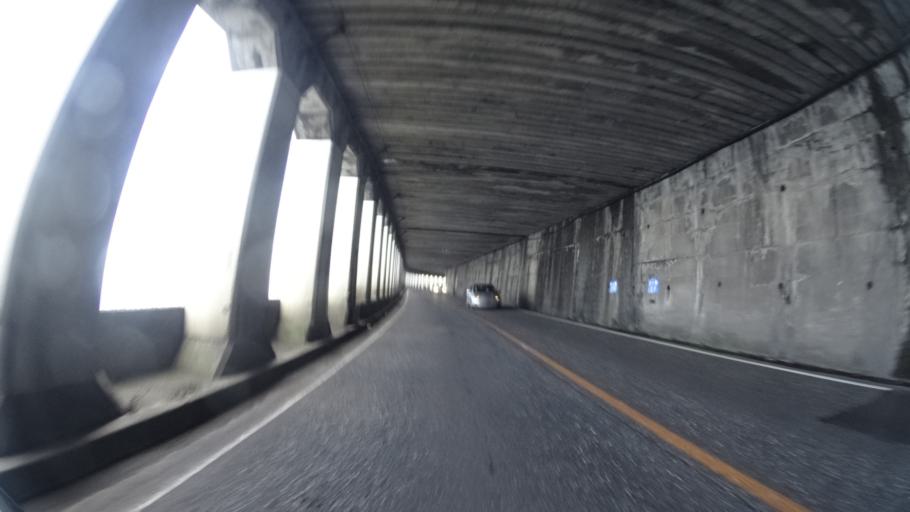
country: JP
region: Niigata
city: Itoigawa
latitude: 36.9895
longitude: 137.6785
